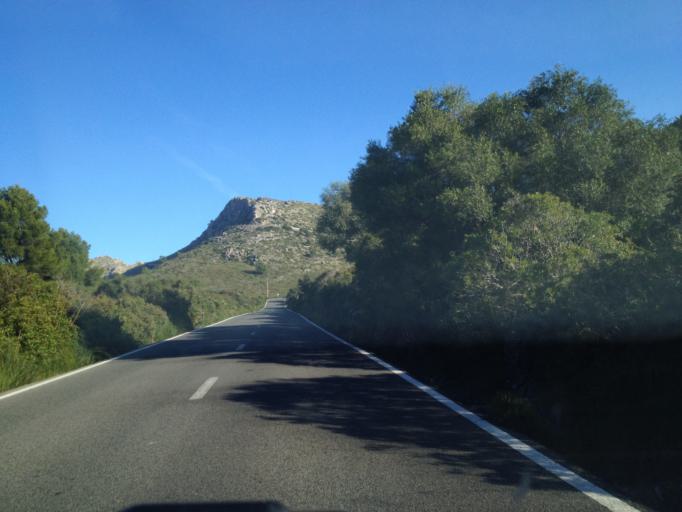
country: ES
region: Balearic Islands
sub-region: Illes Balears
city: Alcudia
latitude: 39.9129
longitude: 3.1028
